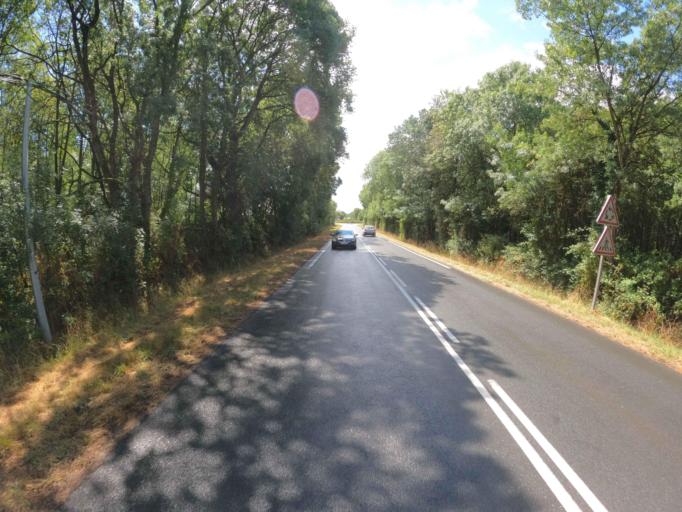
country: FR
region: Pays de la Loire
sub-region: Departement de Maine-et-Loire
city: Feneu
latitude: 47.6141
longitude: -0.5848
